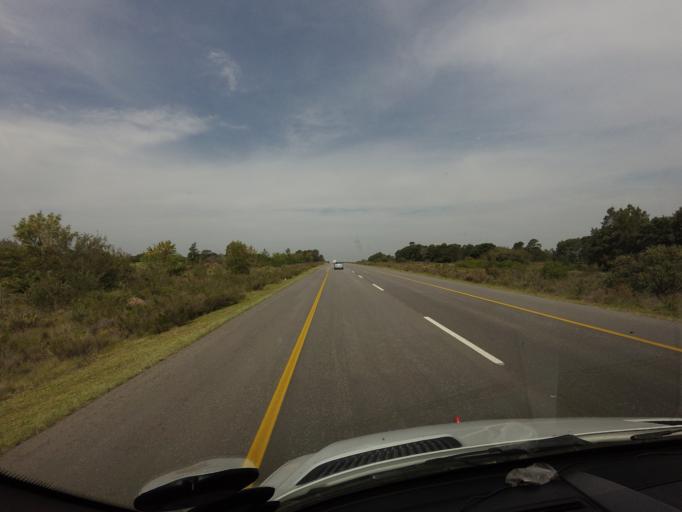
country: ZA
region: Eastern Cape
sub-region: Cacadu District Municipality
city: Kruisfontein
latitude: -33.9978
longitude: 24.7484
